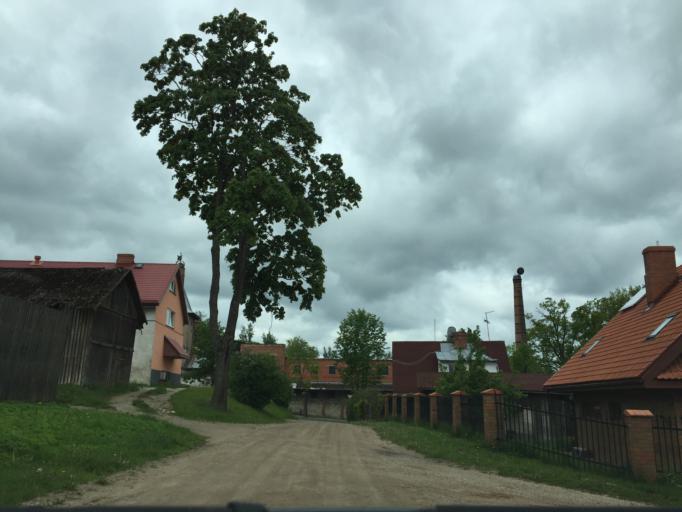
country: LV
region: Cesu Rajons
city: Cesis
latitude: 57.3157
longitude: 25.2719
